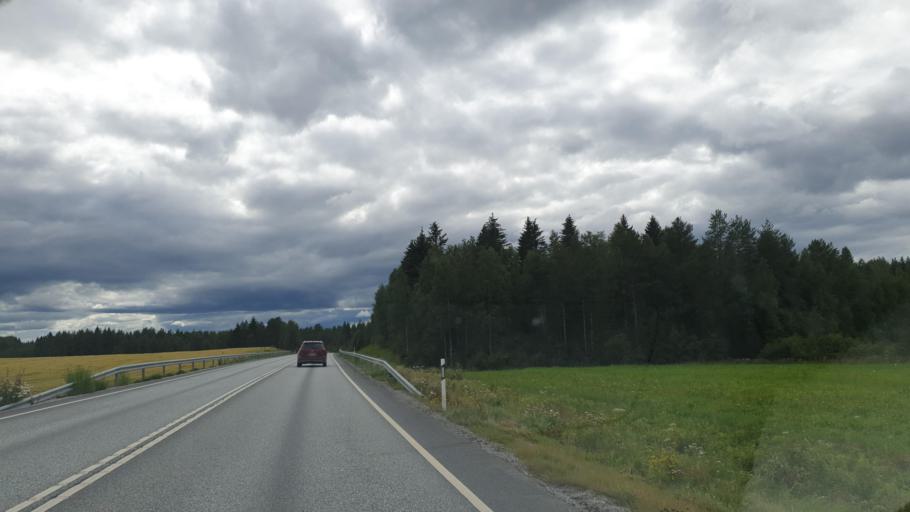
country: FI
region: Northern Savo
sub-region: Ylae-Savo
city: Sonkajaervi
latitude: 63.8421
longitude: 27.4326
